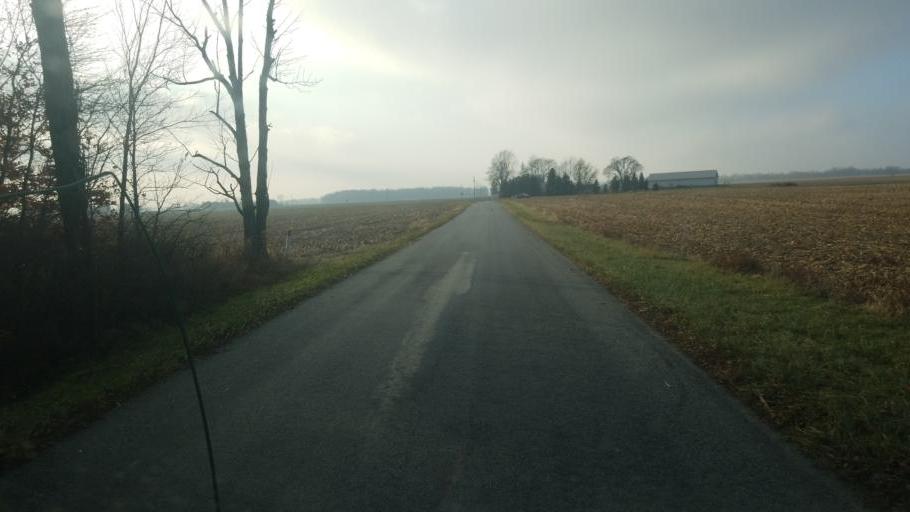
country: US
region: Ohio
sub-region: Hardin County
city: Kenton
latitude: 40.6883
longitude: -83.5826
